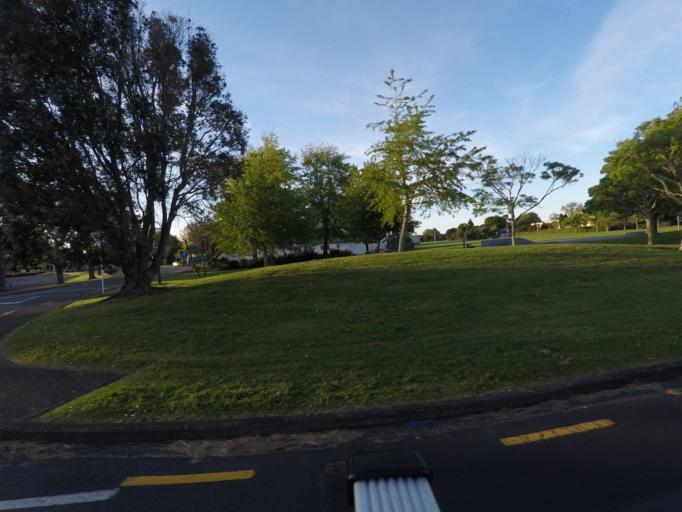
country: NZ
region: Auckland
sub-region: Auckland
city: Rosebank
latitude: -36.8424
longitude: 174.6543
